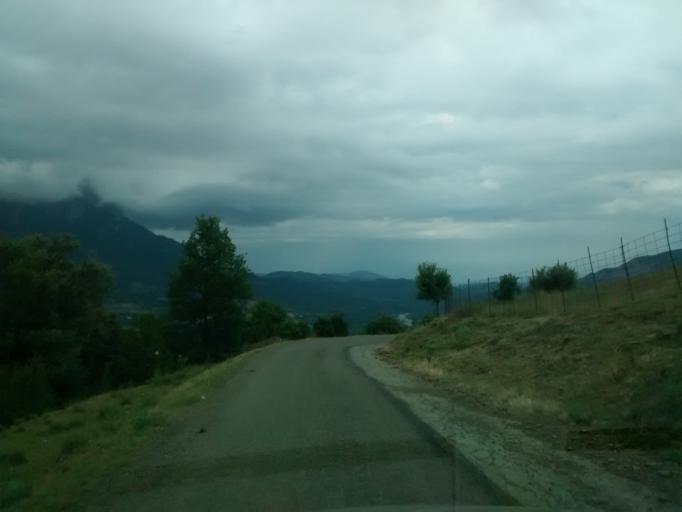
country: ES
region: Aragon
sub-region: Provincia de Huesca
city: Puertolas
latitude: 42.5367
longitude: 0.1329
